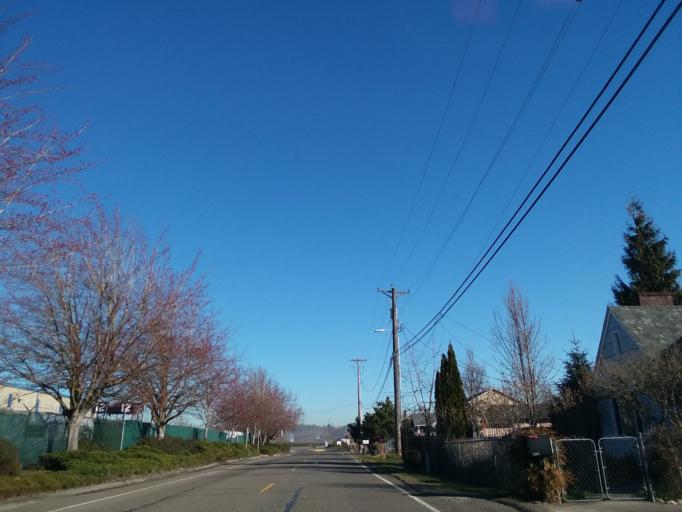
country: US
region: Washington
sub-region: Pierce County
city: Fife
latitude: 47.2450
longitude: -122.3674
